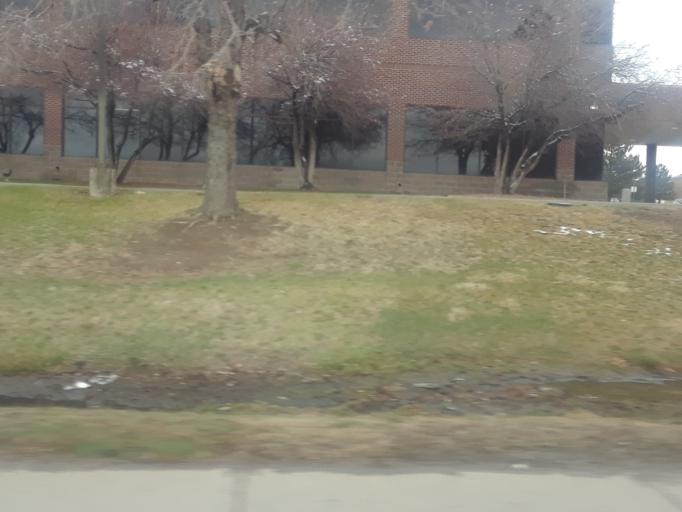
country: US
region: Colorado
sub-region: Arapahoe County
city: Centennial
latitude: 39.5661
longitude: -104.8805
